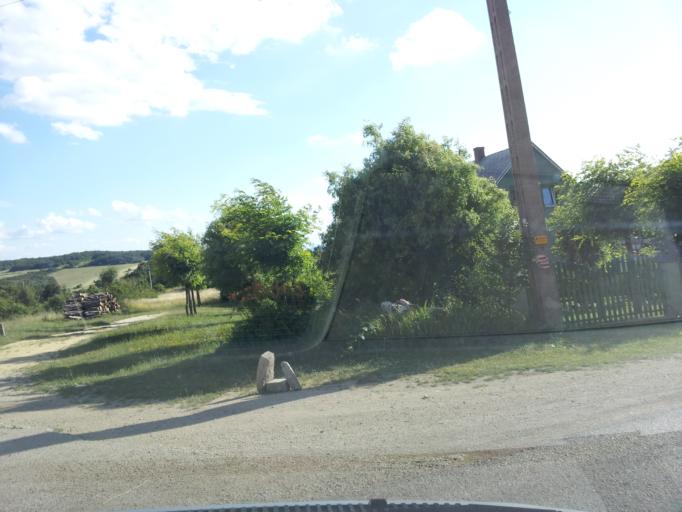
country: HU
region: Veszprem
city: Herend
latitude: 47.1874
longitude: 17.8224
